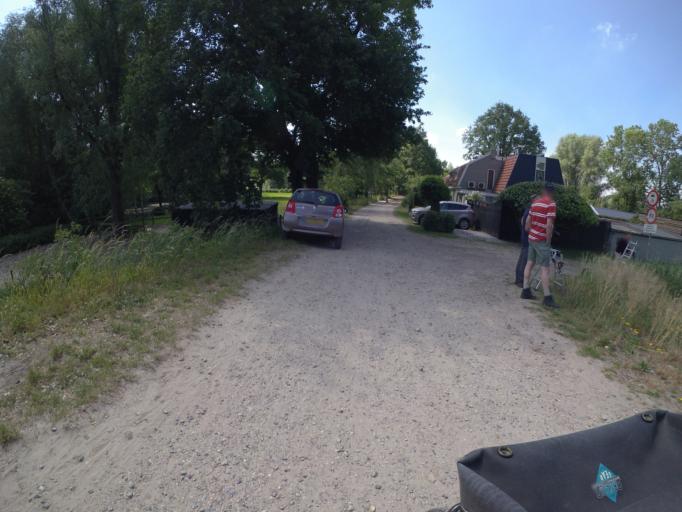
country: NL
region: North Brabant
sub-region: Gemeente Haaren
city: Haaren
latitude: 51.5867
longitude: 5.2421
